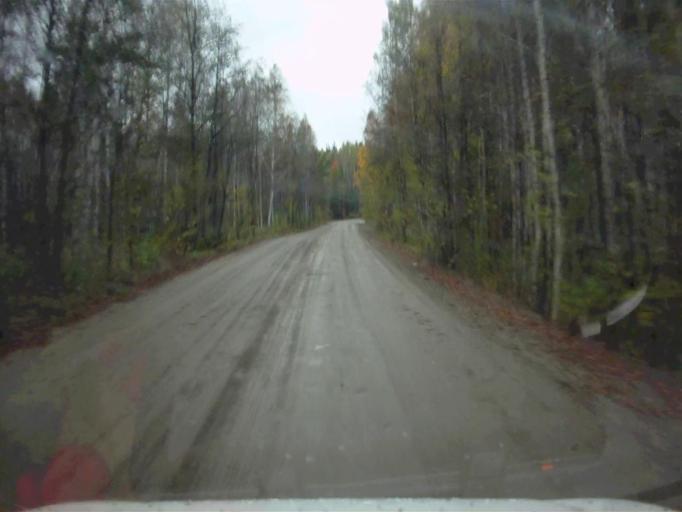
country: RU
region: Chelyabinsk
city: Kyshtym
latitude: 55.8331
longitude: 60.4861
